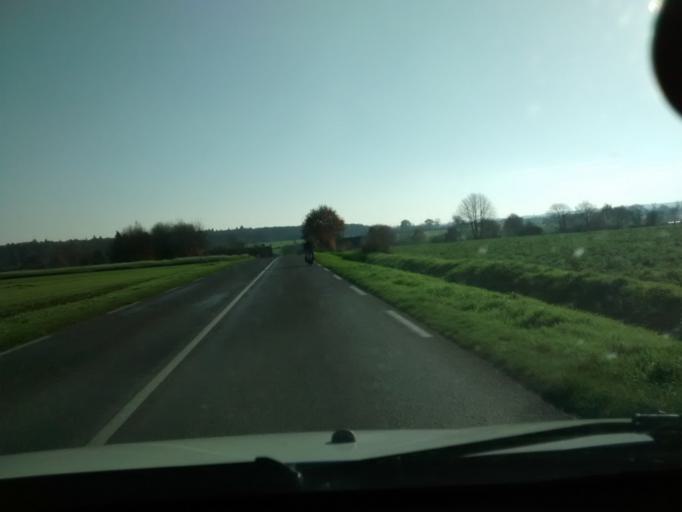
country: FR
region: Brittany
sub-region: Departement d'Ille-et-Vilaine
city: Antrain
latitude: 48.4913
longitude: -1.4684
